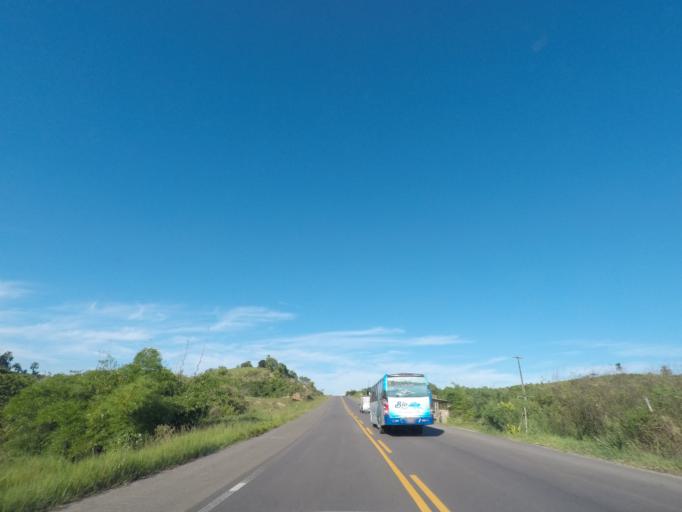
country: BR
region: Bahia
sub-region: Nazare
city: Nazare
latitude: -13.0275
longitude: -38.9915
